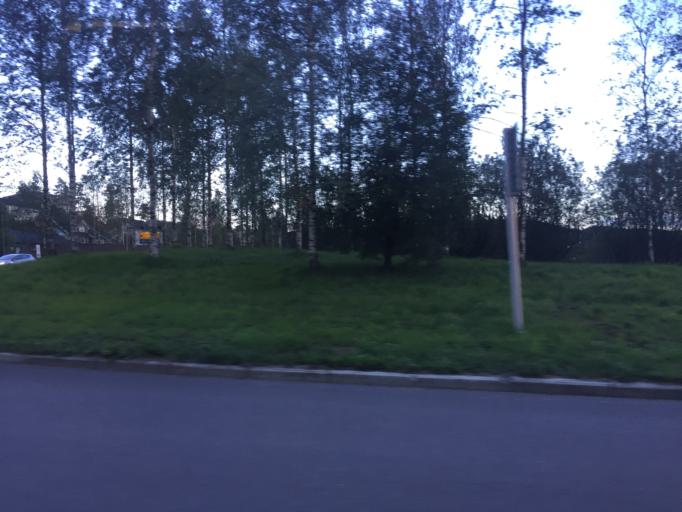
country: NO
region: Akershus
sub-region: Skedsmo
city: Lillestrom
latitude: 59.9408
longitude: 11.0141
